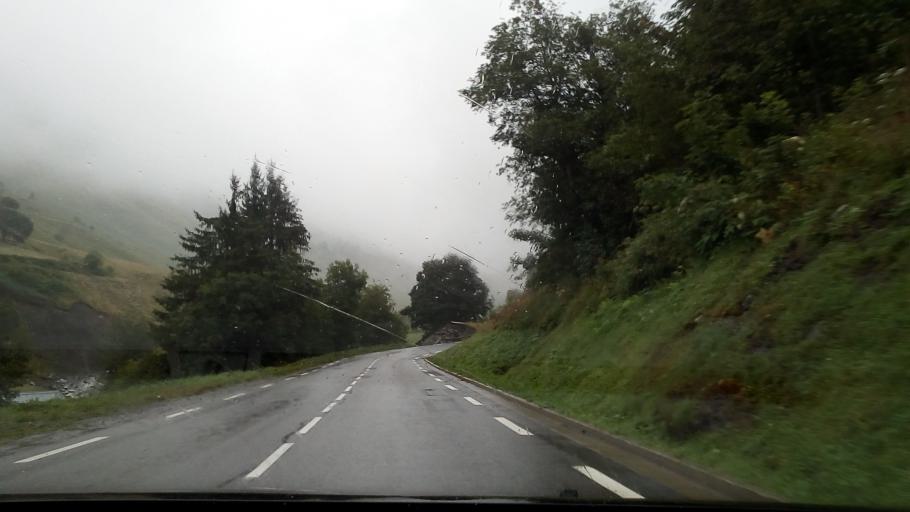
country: FR
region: Midi-Pyrenees
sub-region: Departement des Hautes-Pyrenees
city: Luz-Saint-Sauveur
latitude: 42.9025
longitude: 0.0892
